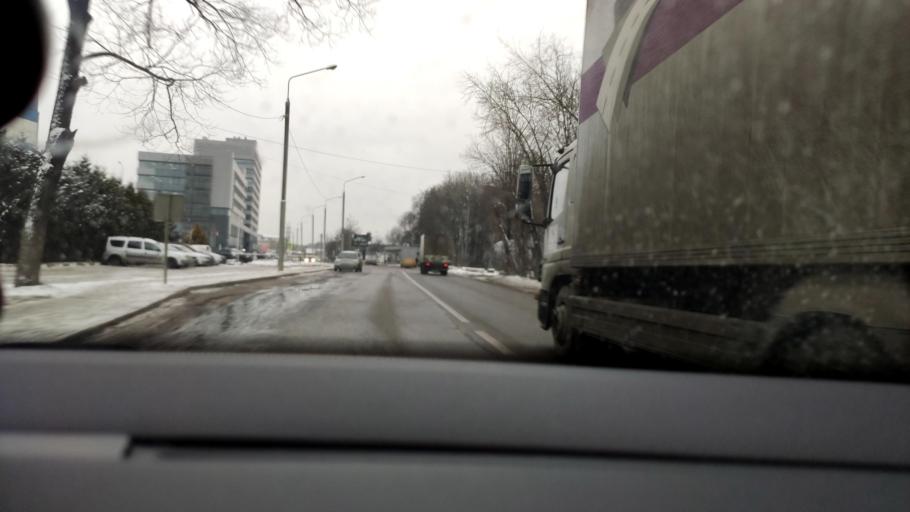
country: RU
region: Moscow
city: Khimki
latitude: 55.9206
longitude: 37.4189
